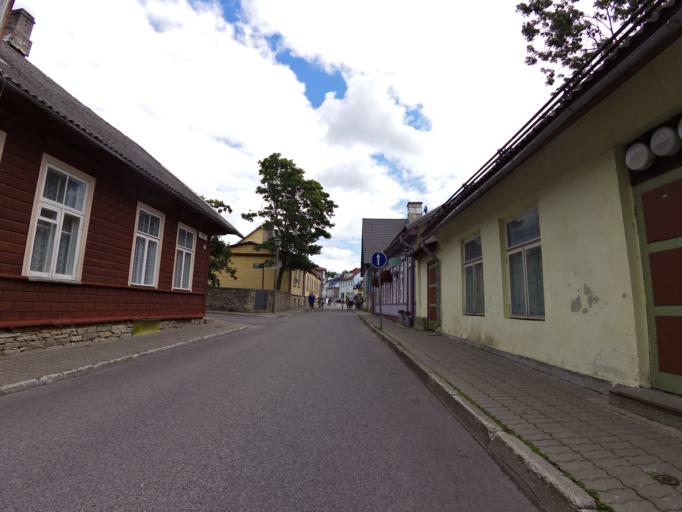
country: EE
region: Laeaene
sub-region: Haapsalu linn
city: Haapsalu
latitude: 58.9485
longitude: 23.5361
